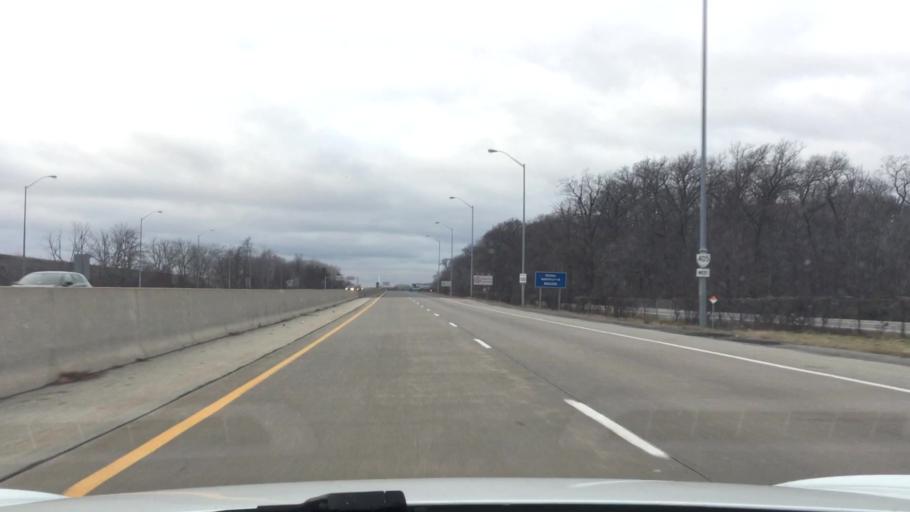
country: US
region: New York
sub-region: Niagara County
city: Lewiston
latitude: 43.1570
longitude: -79.0568
